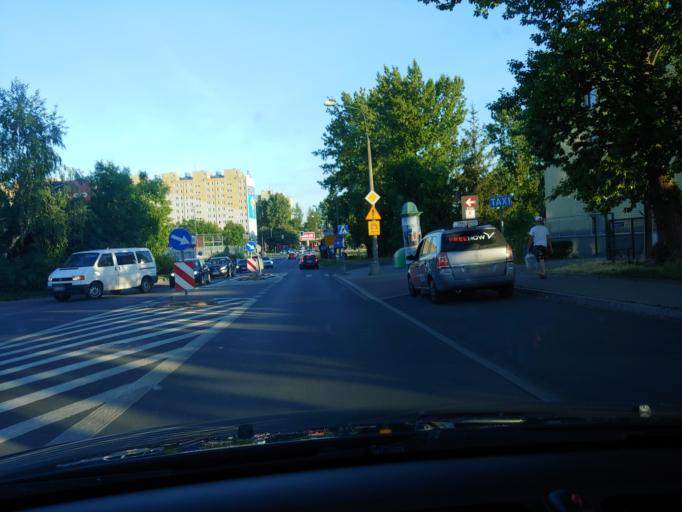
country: PL
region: Lesser Poland Voivodeship
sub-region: Powiat krakowski
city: Zielonki
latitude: 50.0926
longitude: 19.9221
